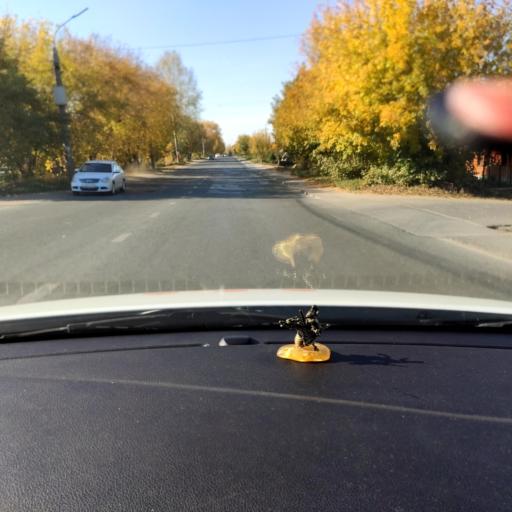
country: RU
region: Tatarstan
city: Verkhniy Uslon
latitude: 55.8001
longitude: 49.0326
